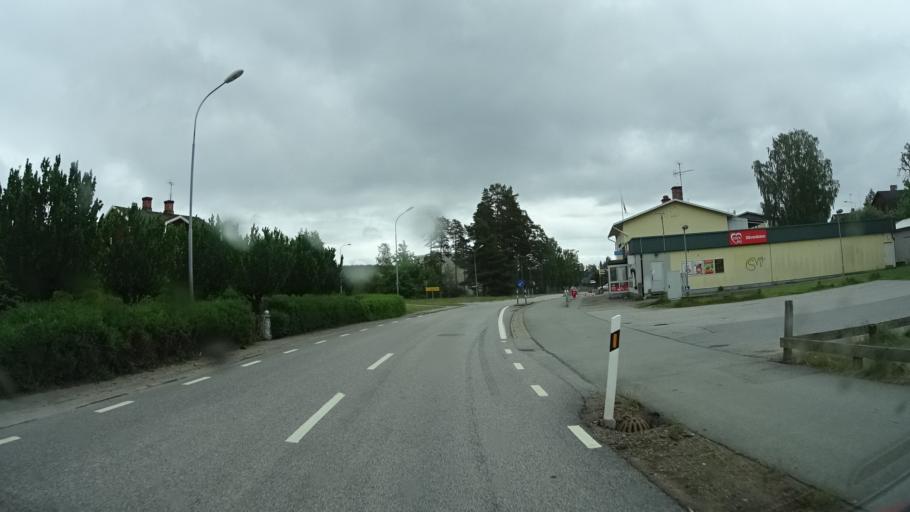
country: SE
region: Kalmar
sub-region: Hultsfreds Kommun
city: Hultsfred
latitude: 57.5434
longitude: 15.7503
